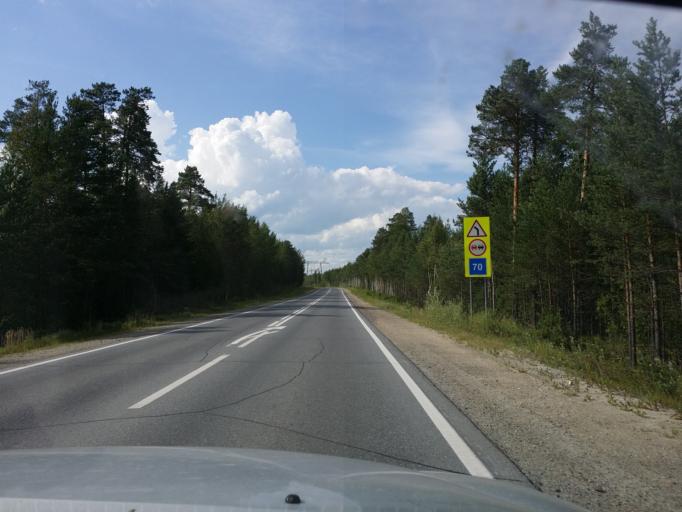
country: RU
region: Khanty-Mansiyskiy Avtonomnyy Okrug
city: Megion
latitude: 61.1558
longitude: 75.7365
